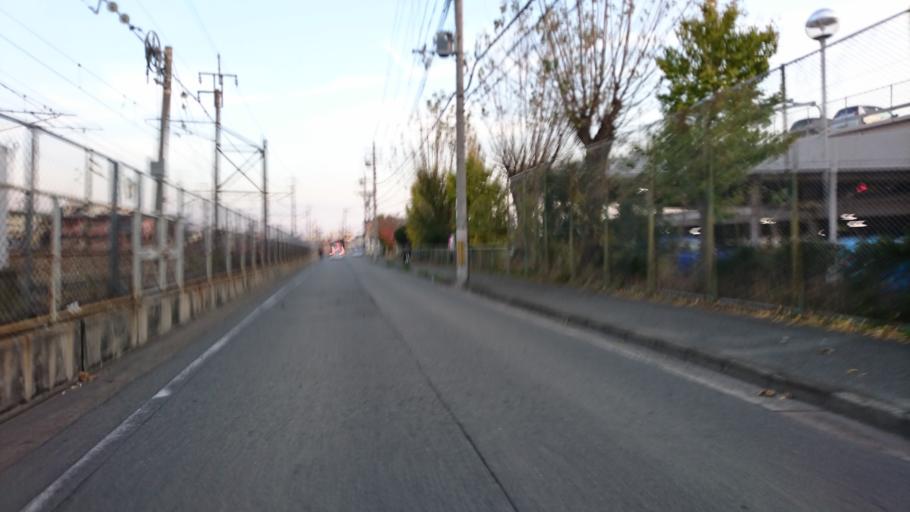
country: JP
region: Hyogo
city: Kakogawacho-honmachi
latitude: 34.7505
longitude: 134.8637
